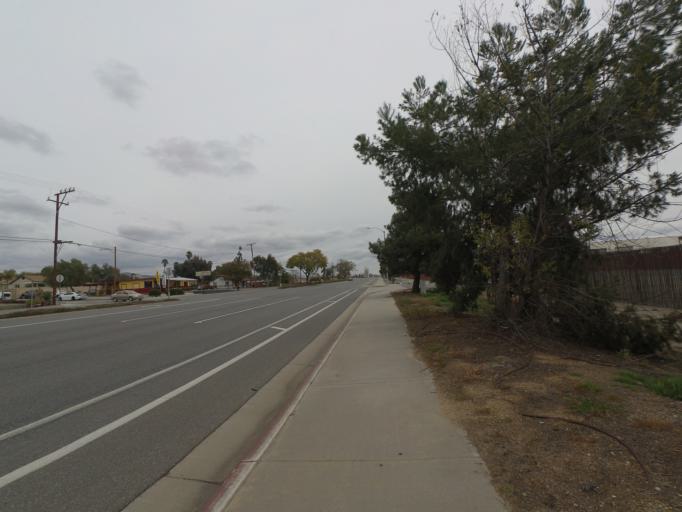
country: US
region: California
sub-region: Riverside County
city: March Air Force Base
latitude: 33.9167
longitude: -117.2767
